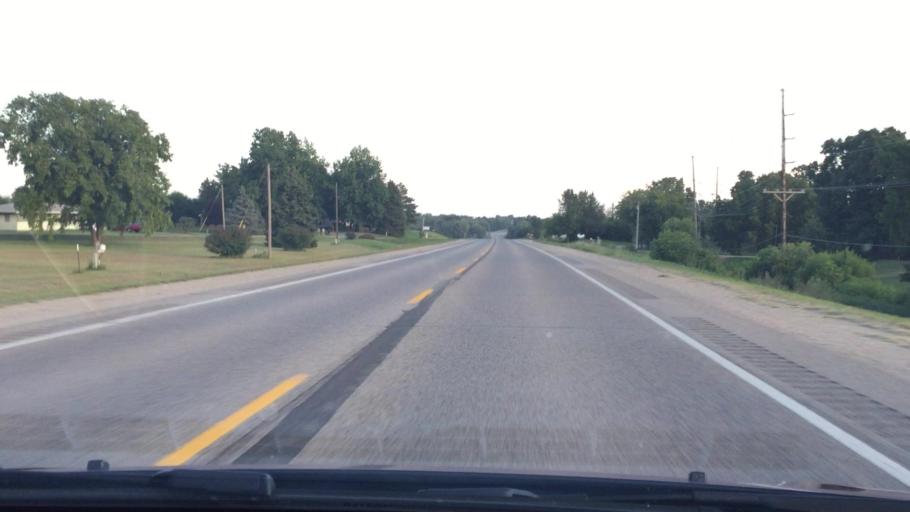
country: US
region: Iowa
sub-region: Muscatine County
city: Muscatine
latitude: 41.4695
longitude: -91.0362
